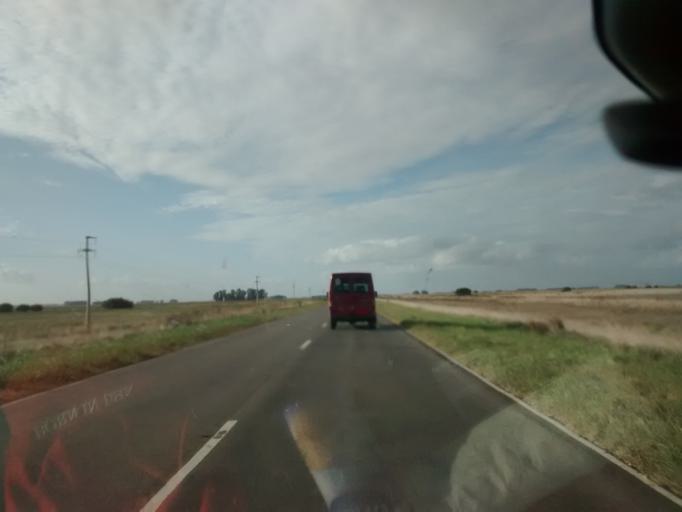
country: AR
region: Buenos Aires
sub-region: Partido de Ayacucho
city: Ayacucho
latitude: -36.8141
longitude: -58.5661
